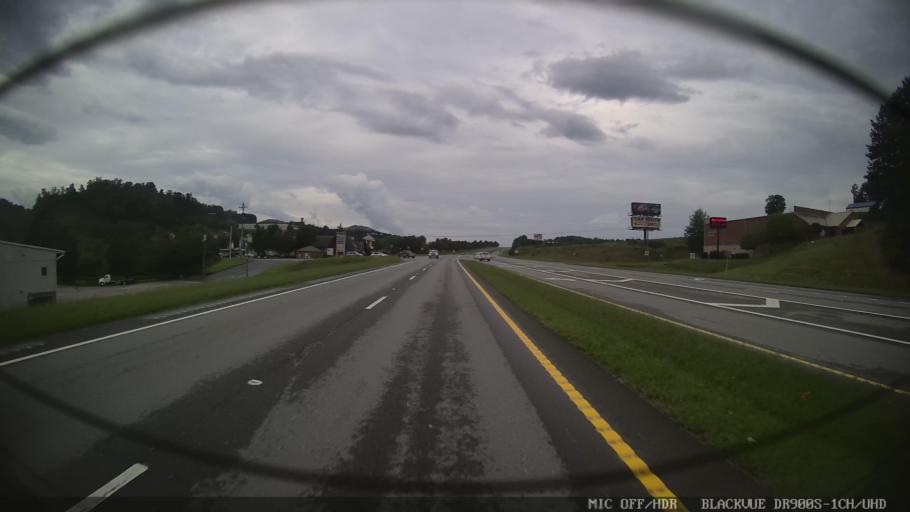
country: US
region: Georgia
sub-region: Gilmer County
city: Ellijay
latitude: 34.6654
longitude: -84.4866
